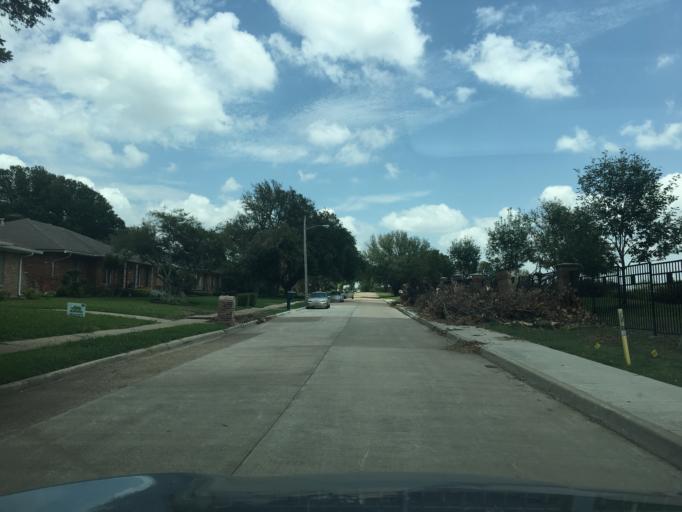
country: US
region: Texas
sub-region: Dallas County
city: Richardson
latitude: 32.9077
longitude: -96.7538
